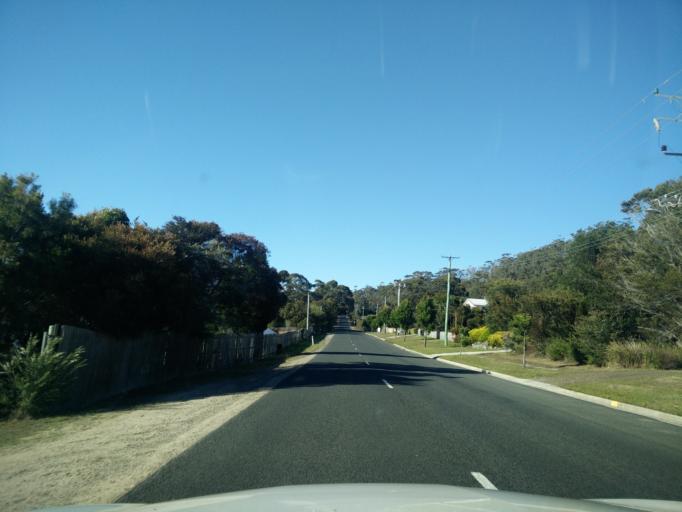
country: AU
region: Tasmania
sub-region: Break O'Day
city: St Helens
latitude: -41.8810
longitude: 148.3021
